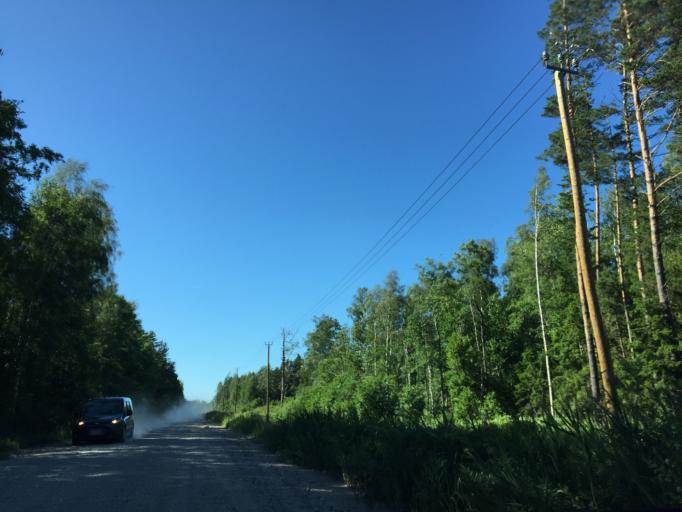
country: LV
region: Ventspils
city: Ventspils
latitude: 57.5563
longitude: 21.7353
